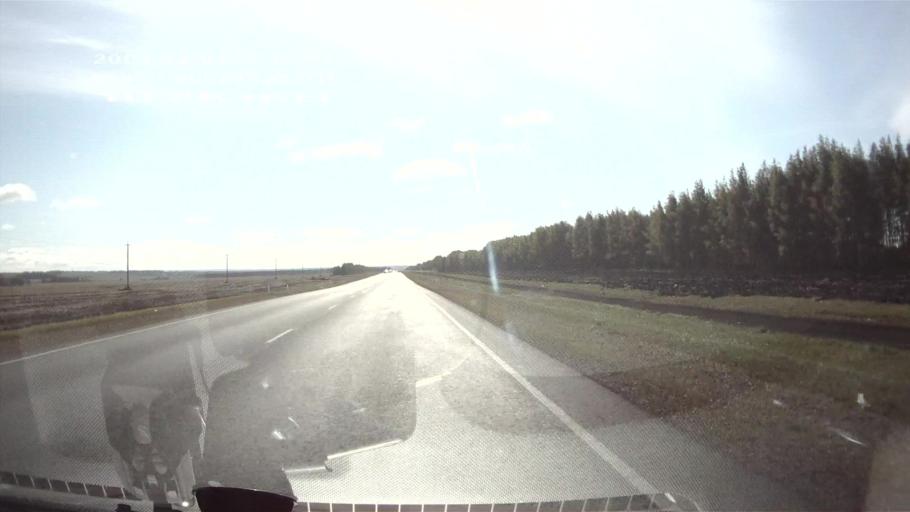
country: RU
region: Ulyanovsk
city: Tsil'na
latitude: 54.5709
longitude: 47.9077
